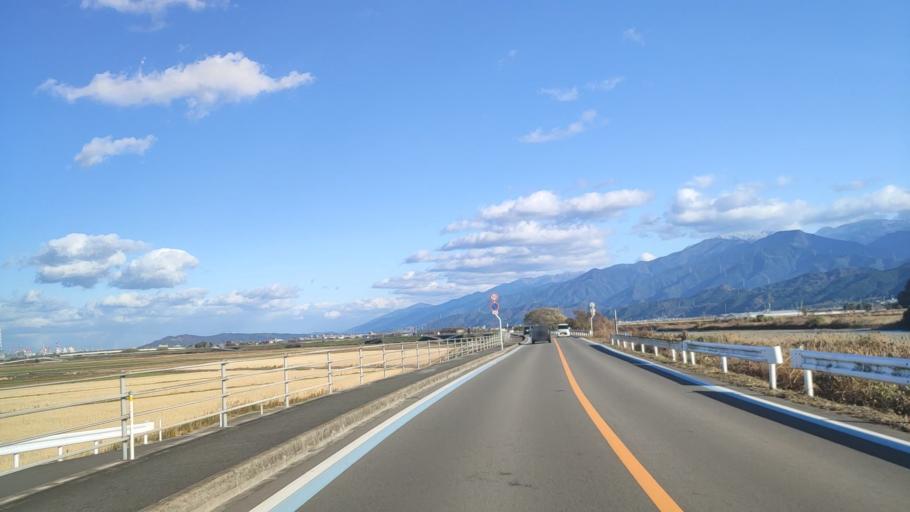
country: JP
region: Ehime
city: Saijo
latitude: 33.9069
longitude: 133.1198
